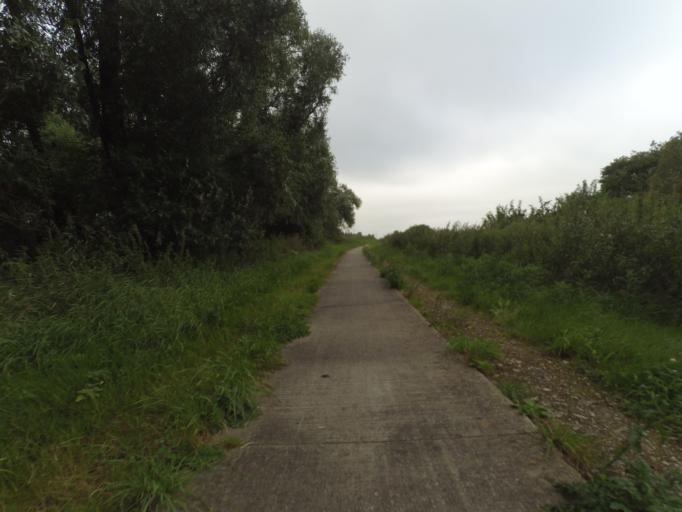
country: NL
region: Flevoland
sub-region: Gemeente Lelystad
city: Lelystad
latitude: 52.4368
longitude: 5.4182
